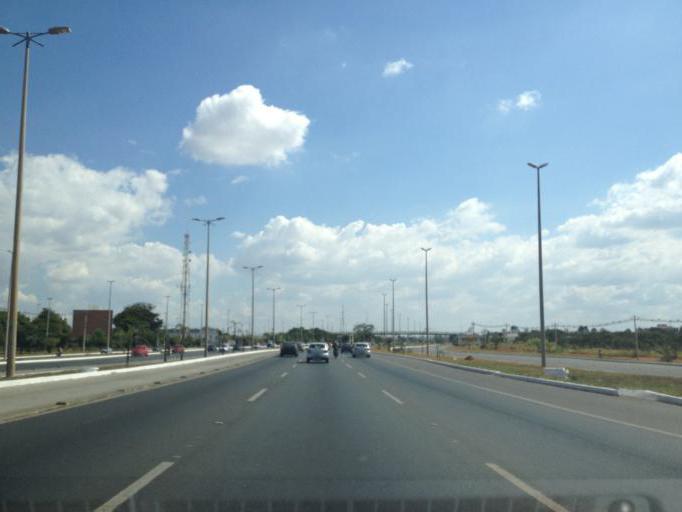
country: BR
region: Federal District
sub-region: Brasilia
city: Brasilia
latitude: -15.8121
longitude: -47.9809
